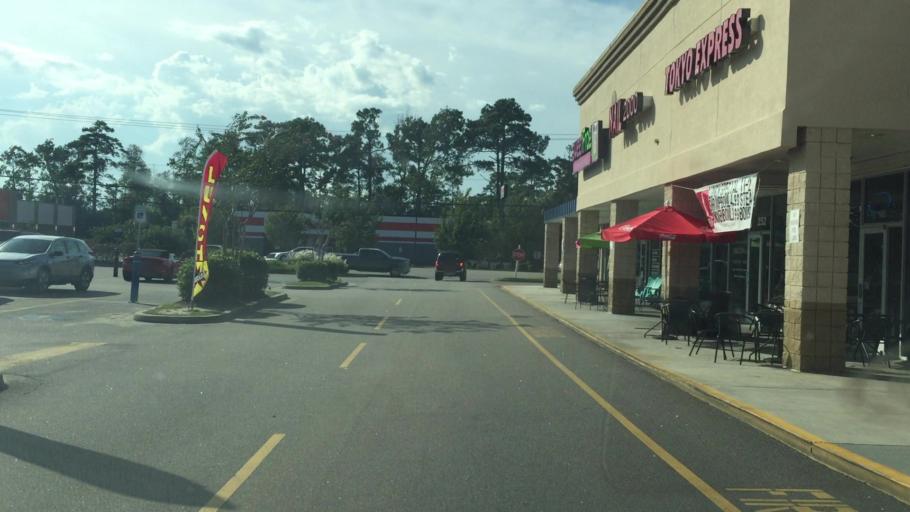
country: US
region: South Carolina
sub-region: Horry County
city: North Myrtle Beach
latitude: 33.8308
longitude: -78.6756
